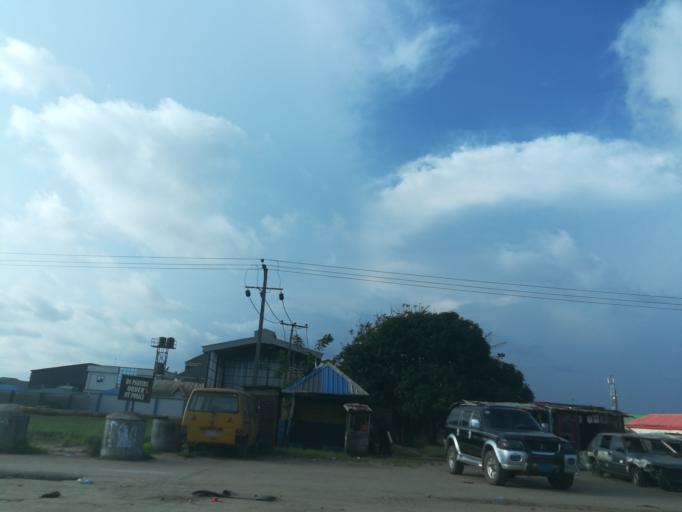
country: NG
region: Ogun
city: Ado Odo
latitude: 6.4854
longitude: 3.0561
